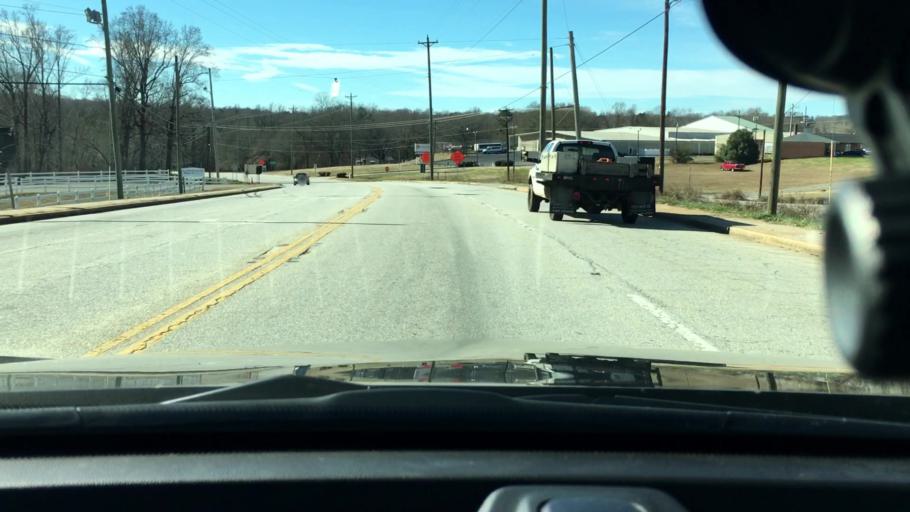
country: US
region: South Carolina
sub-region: Cherokee County
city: East Gaffney
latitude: 35.1017
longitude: -81.6253
